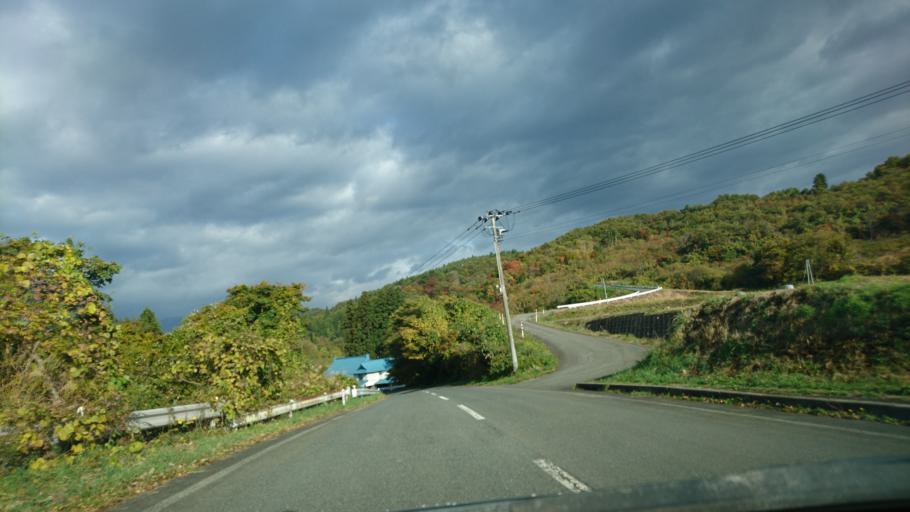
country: JP
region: Iwate
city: Mizusawa
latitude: 39.0868
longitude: 140.9852
